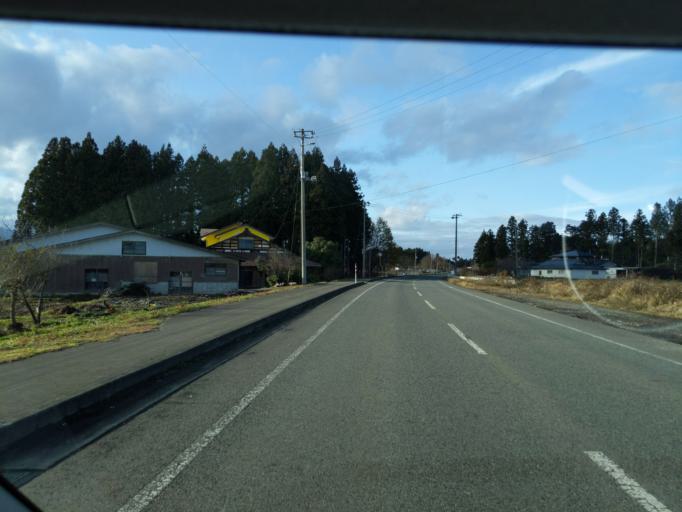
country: JP
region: Iwate
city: Mizusawa
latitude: 39.1911
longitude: 141.0738
